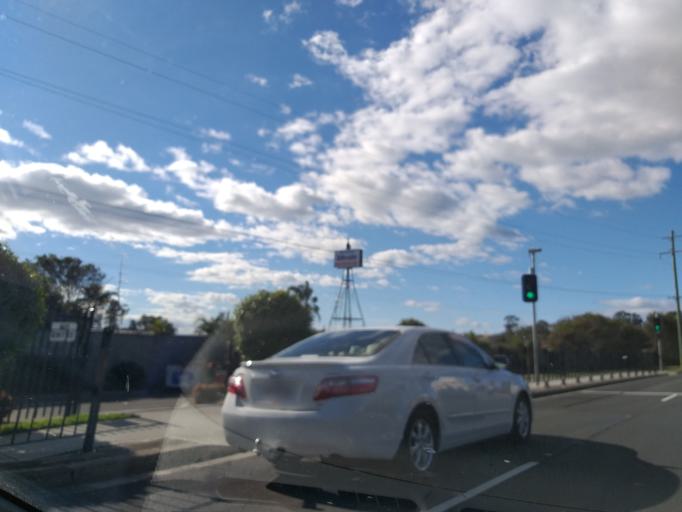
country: AU
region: New South Wales
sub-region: Shellharbour
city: Barrack Heights
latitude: -34.5628
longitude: 150.8333
